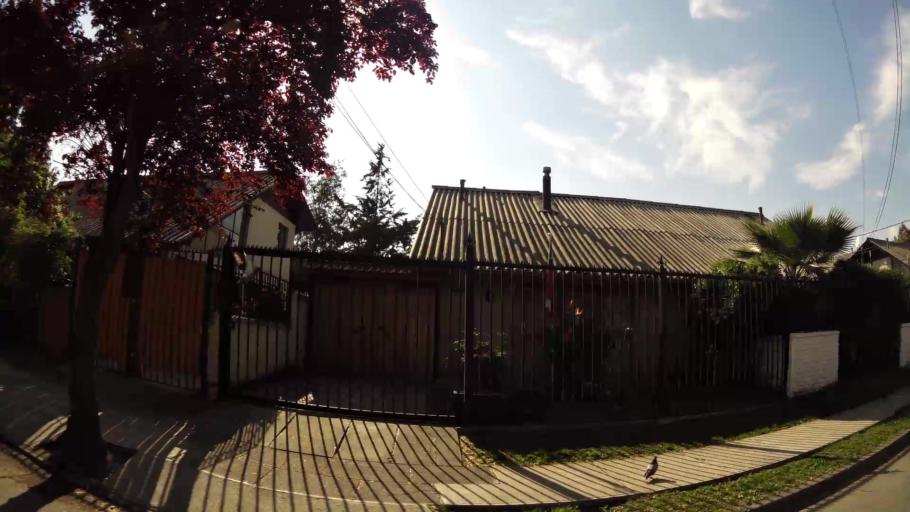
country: CL
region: Santiago Metropolitan
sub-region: Provincia de Santiago
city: La Pintana
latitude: -33.5597
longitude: -70.5988
